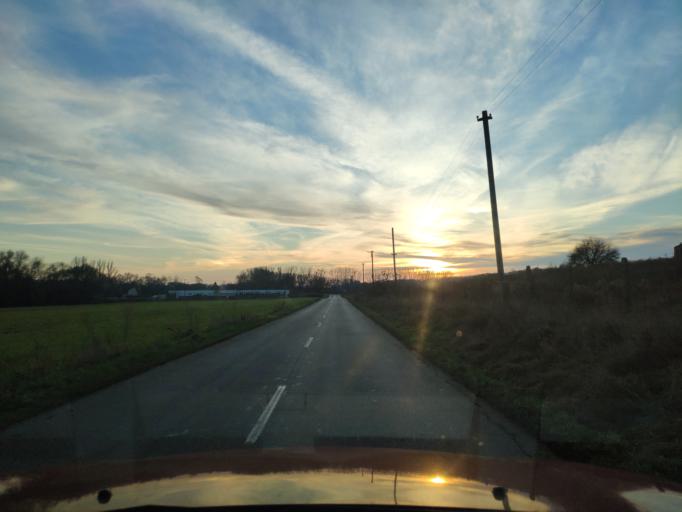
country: SK
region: Kosicky
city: Kosice
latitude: 48.6624
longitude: 21.3943
